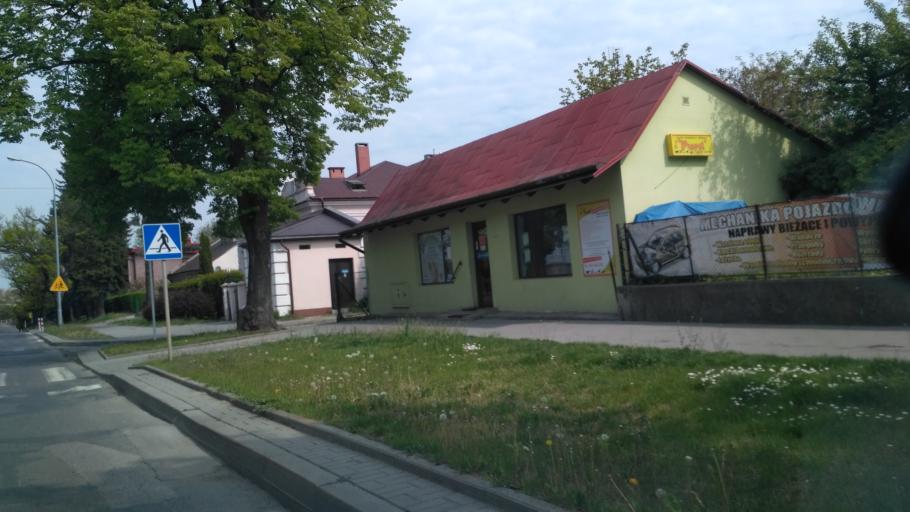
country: PL
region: Subcarpathian Voivodeship
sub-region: Powiat jaroslawski
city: Jaroslaw
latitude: 50.0206
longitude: 22.6762
